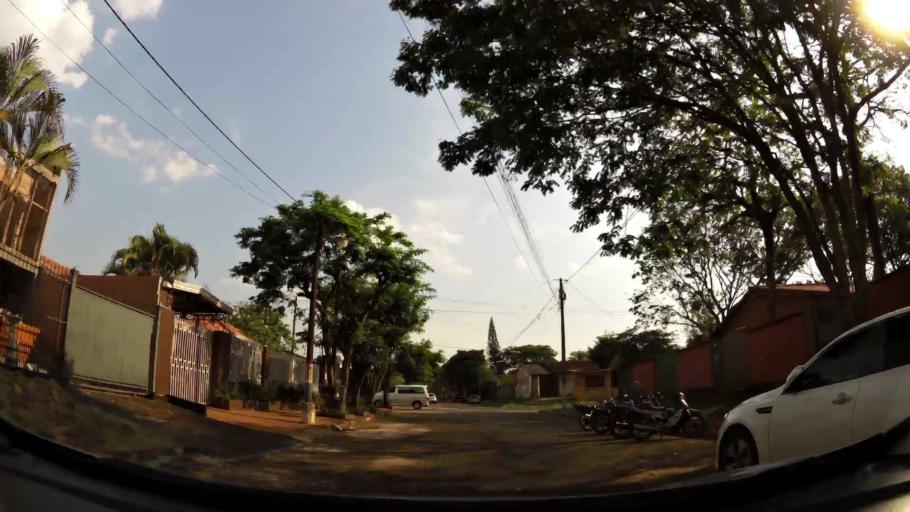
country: PY
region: Alto Parana
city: Presidente Franco
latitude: -25.5299
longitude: -54.6242
